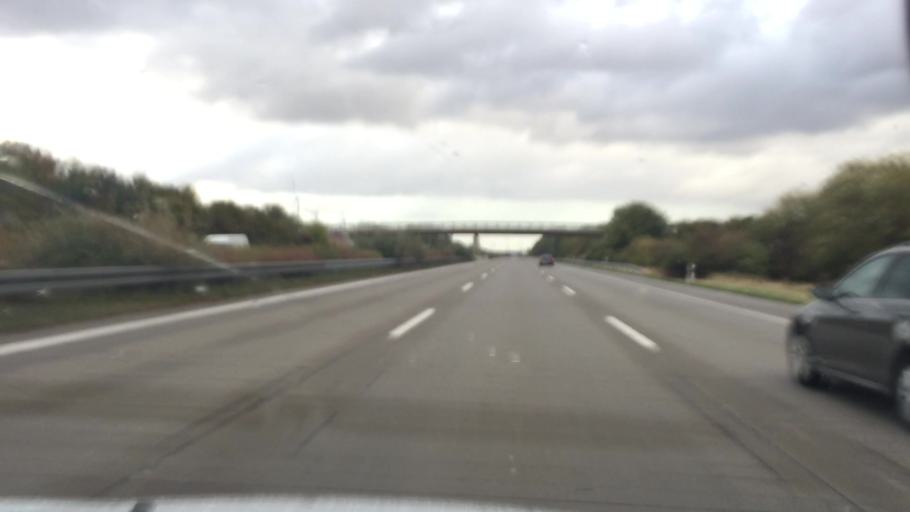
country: DE
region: Saxony-Anhalt
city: Eichenbarleben
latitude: 52.1892
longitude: 11.3298
